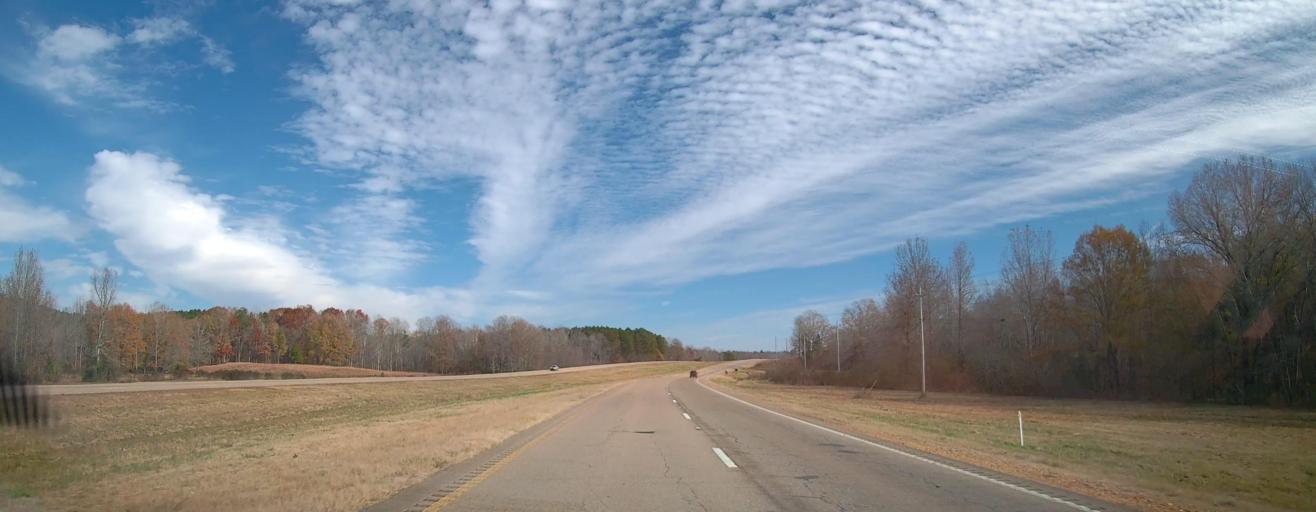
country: US
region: Mississippi
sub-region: Alcorn County
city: Corinth
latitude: 34.9361
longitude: -88.7389
